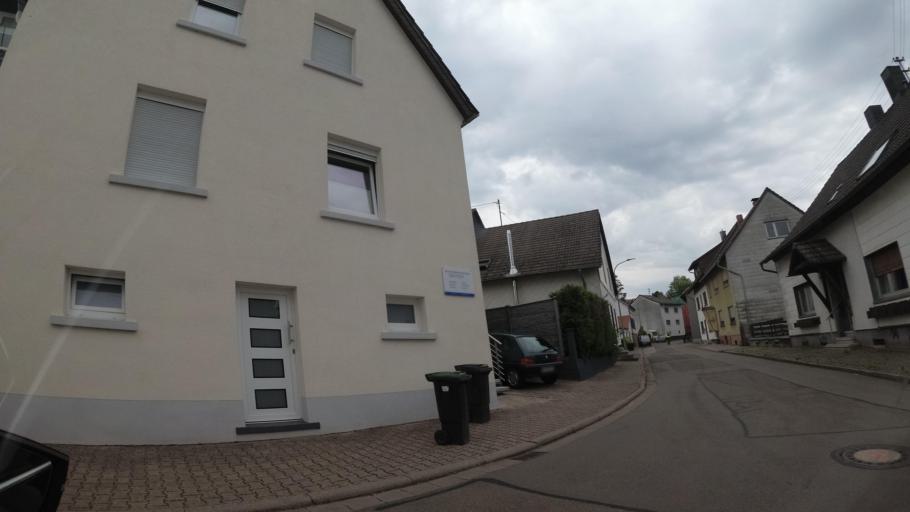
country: DE
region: Rheinland-Pfalz
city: Gries
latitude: 49.4193
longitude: 7.3963
